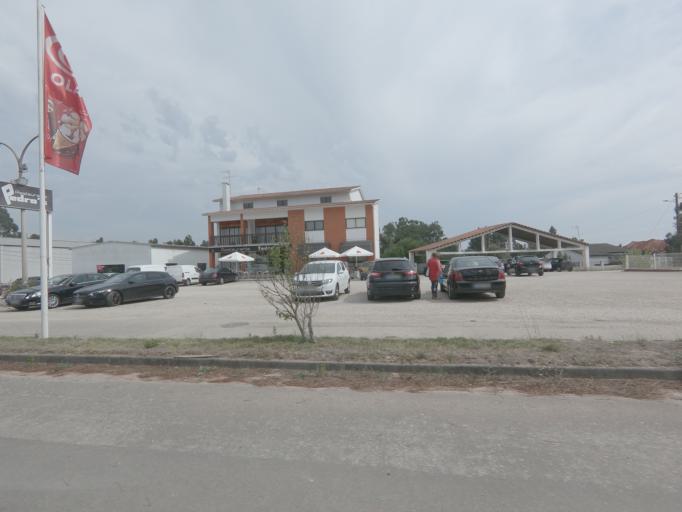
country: PT
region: Leiria
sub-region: Pombal
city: Pombal
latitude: 39.8914
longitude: -8.6617
